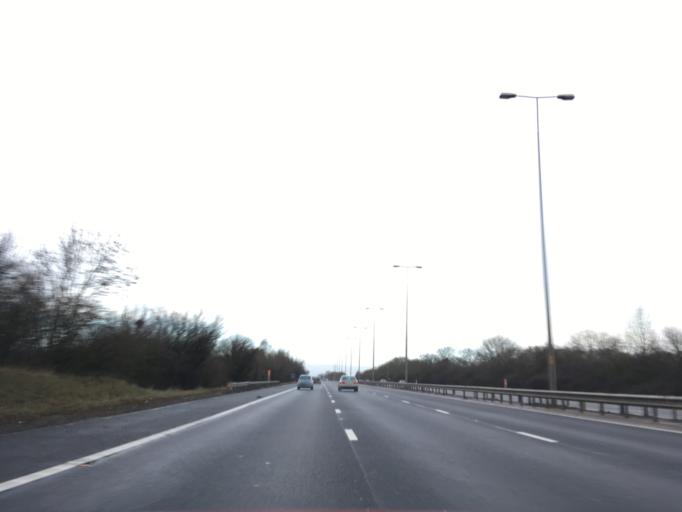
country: GB
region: England
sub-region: Worcestershire
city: Kempsey
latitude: 52.1210
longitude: -2.1990
